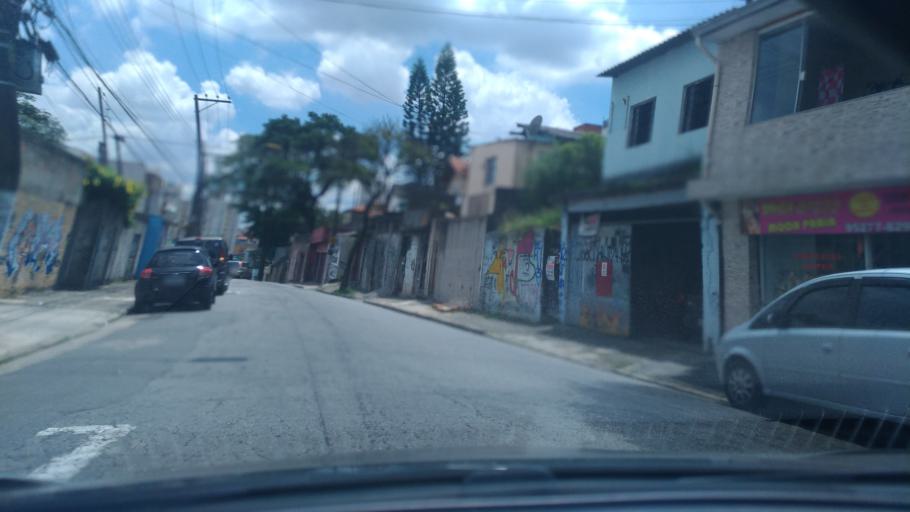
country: BR
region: Sao Paulo
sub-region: Santo Andre
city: Santo Andre
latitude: -23.6973
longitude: -46.5043
